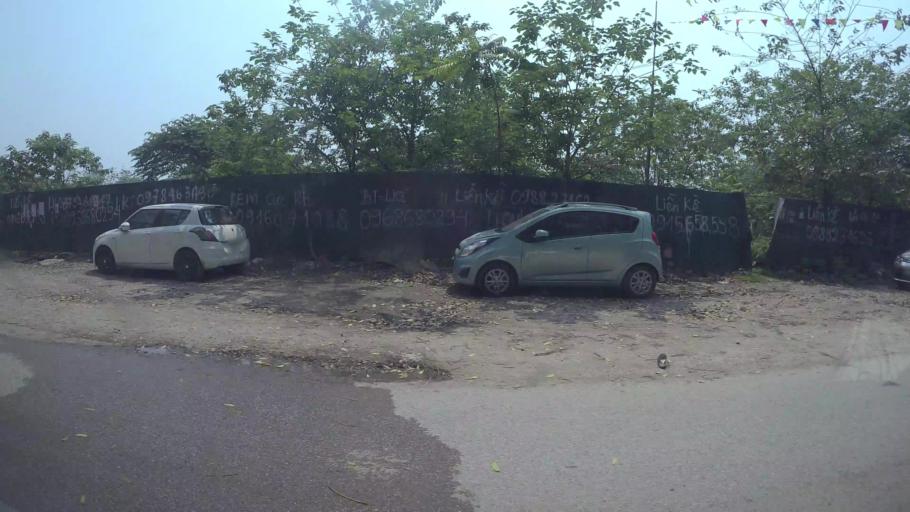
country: VN
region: Ha Noi
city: Ha Dong
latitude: 20.9909
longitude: 105.7634
